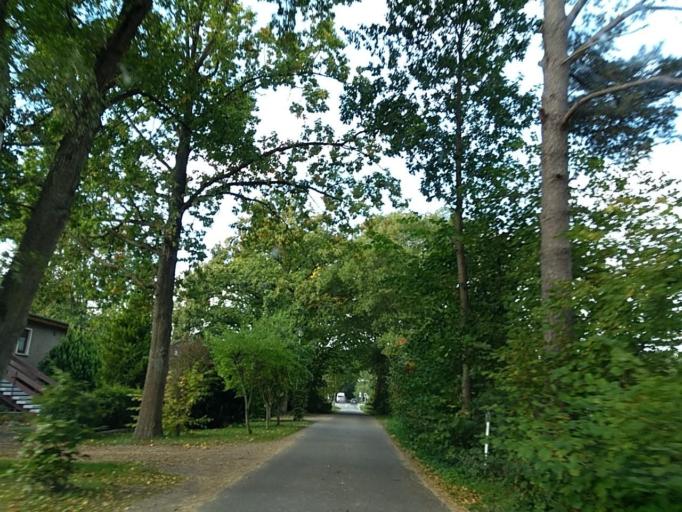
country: DE
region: Mecklenburg-Vorpommern
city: Rovershagen
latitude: 54.1839
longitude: 12.2479
